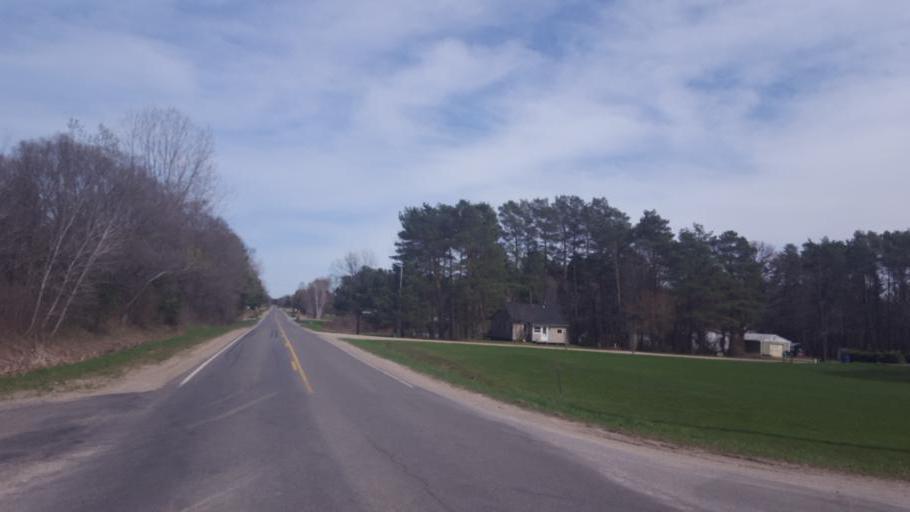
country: US
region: Michigan
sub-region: Gladwin County
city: Gladwin
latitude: 44.0095
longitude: -84.5252
